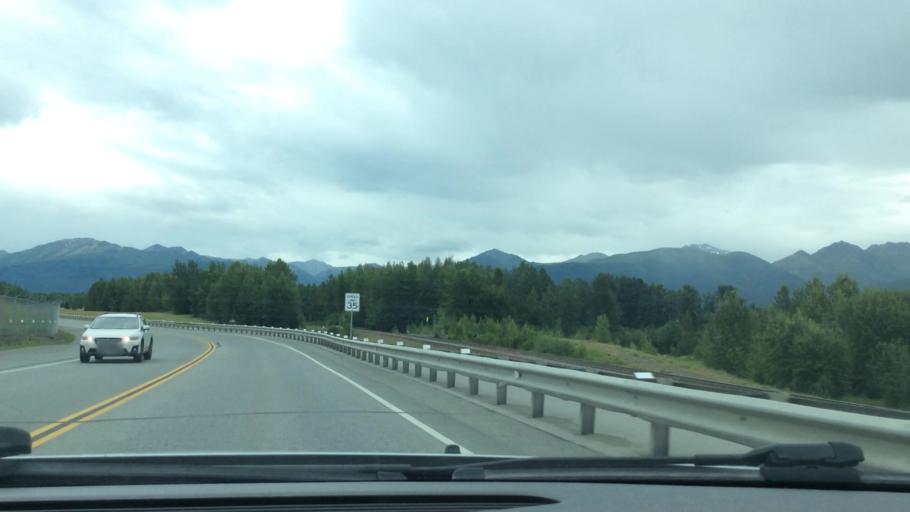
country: US
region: Alaska
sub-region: Anchorage Municipality
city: Anchorage
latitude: 61.2394
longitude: -149.7949
